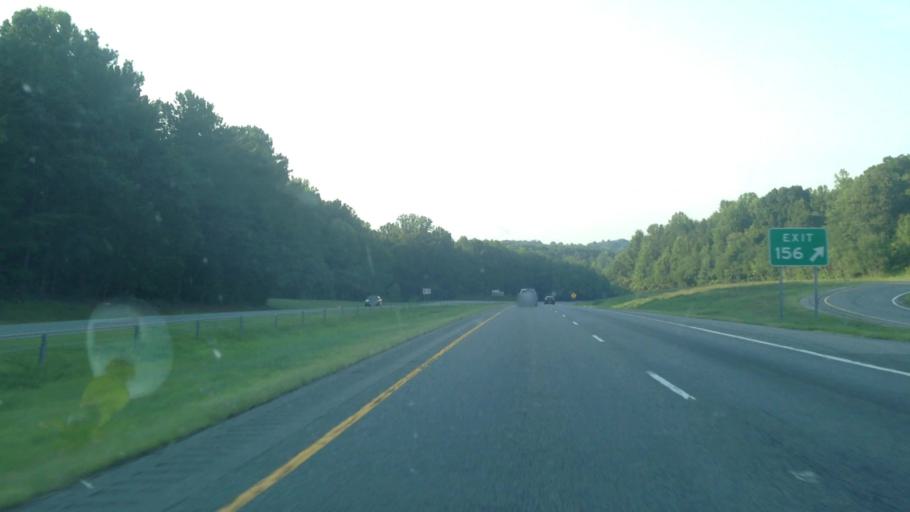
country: US
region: North Carolina
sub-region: Rockingham County
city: Reidsville
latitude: 36.4012
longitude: -79.5977
